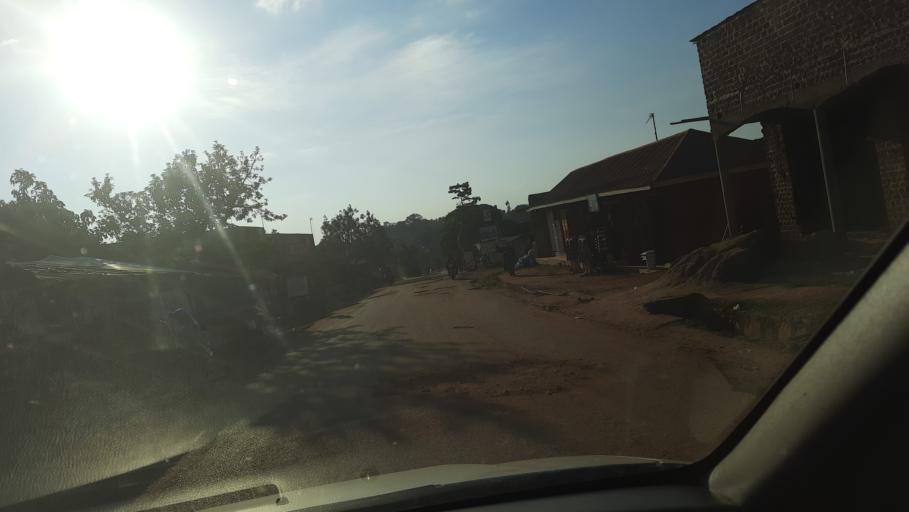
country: UG
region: Central Region
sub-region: Mukono District
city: Mukono
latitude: 0.3705
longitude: 32.7541
